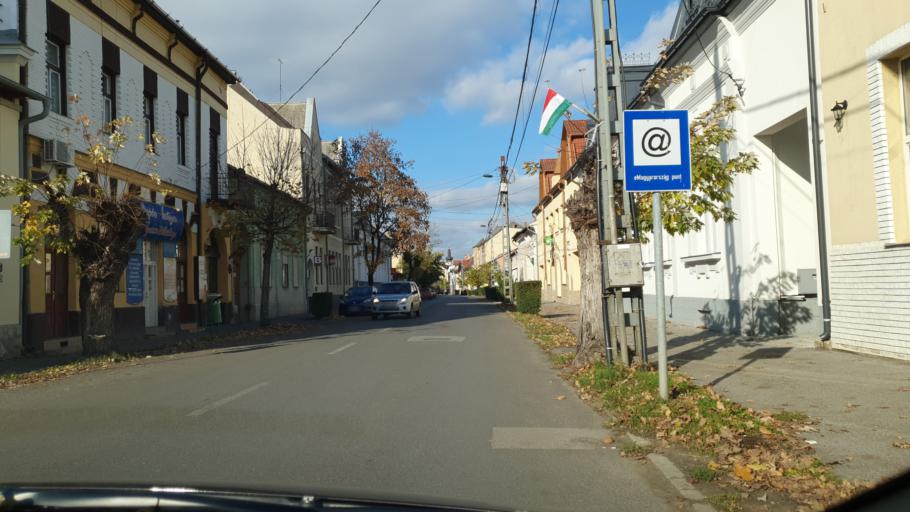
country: HU
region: Szabolcs-Szatmar-Bereg
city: Kisvarda
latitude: 48.2213
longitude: 22.0797
